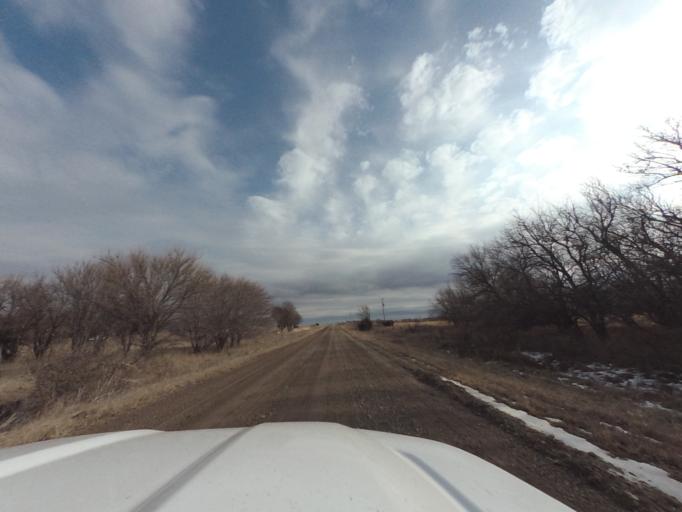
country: US
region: Kansas
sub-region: Chase County
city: Cottonwood Falls
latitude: 38.2170
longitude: -96.6951
